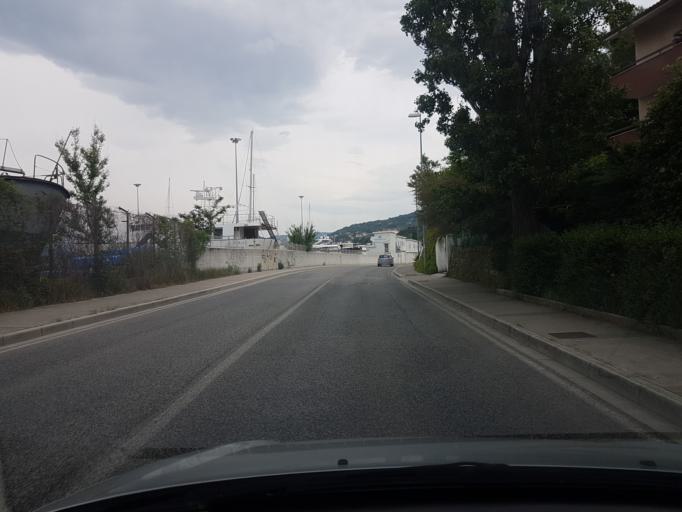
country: IT
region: Friuli Venezia Giulia
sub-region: Provincia di Trieste
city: Muggia
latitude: 45.6031
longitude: 13.7749
